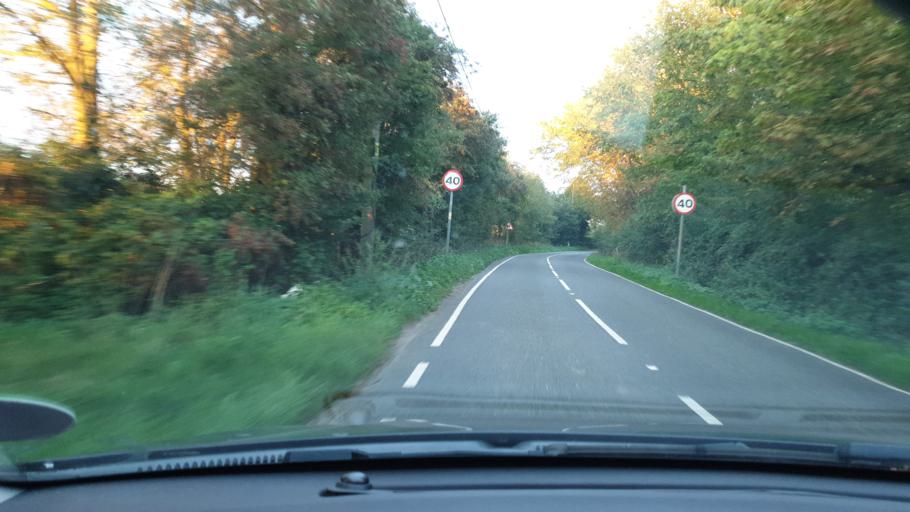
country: GB
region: England
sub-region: Essex
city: Alresford
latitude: 51.9062
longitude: 0.9995
